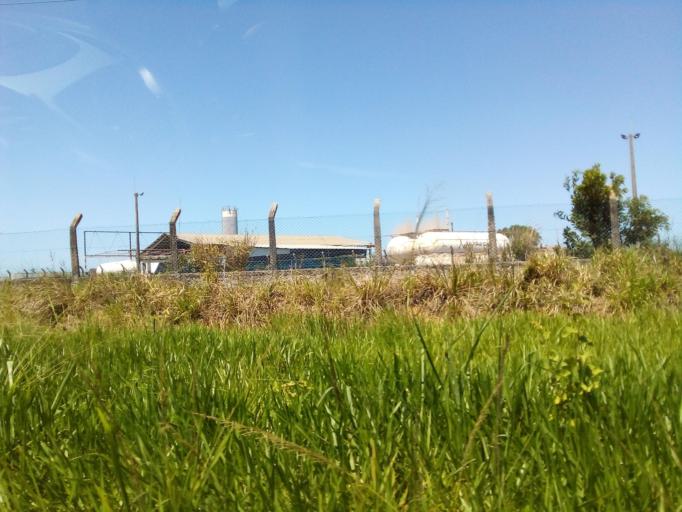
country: BR
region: Espirito Santo
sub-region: Aracruz
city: Aracruz
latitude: -19.8232
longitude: -40.0677
